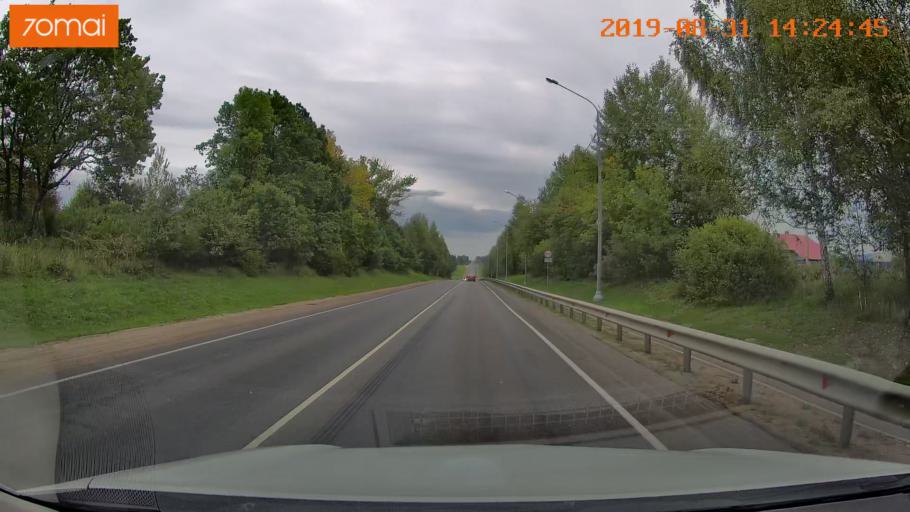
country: RU
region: Smolensk
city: Yekimovichi
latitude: 54.1047
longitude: 33.2612
